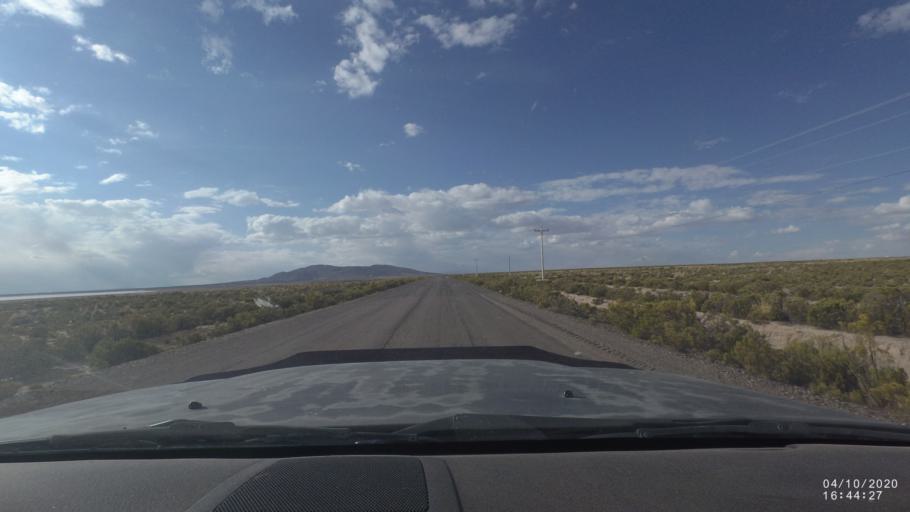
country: BO
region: Oruro
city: Poopo
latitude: -18.6837
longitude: -67.5593
